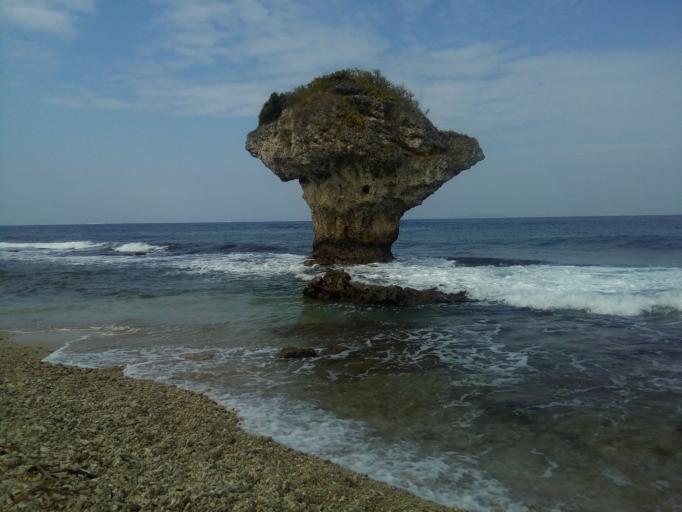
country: TW
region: Kaohsiung
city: Kaohsiung
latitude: 22.3554
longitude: 120.3809
